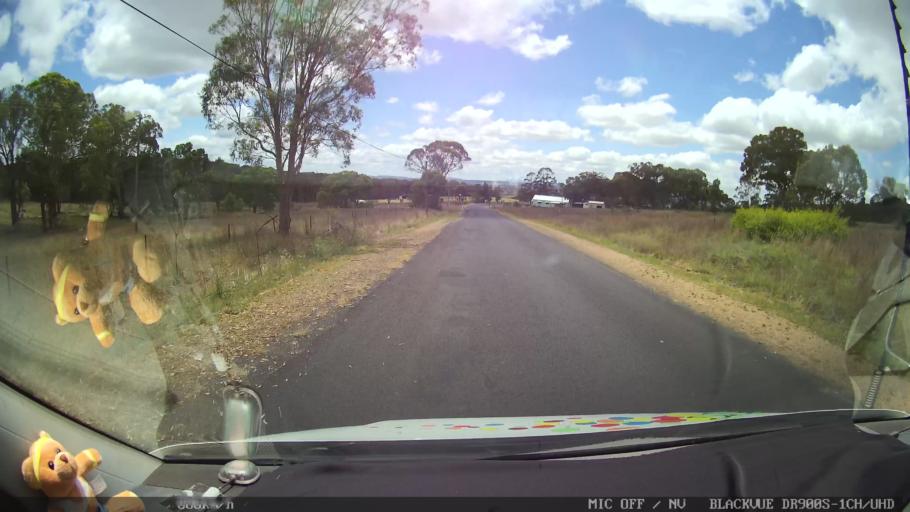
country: AU
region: New South Wales
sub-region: Glen Innes Severn
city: Glen Innes
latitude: -29.4290
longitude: 151.6450
